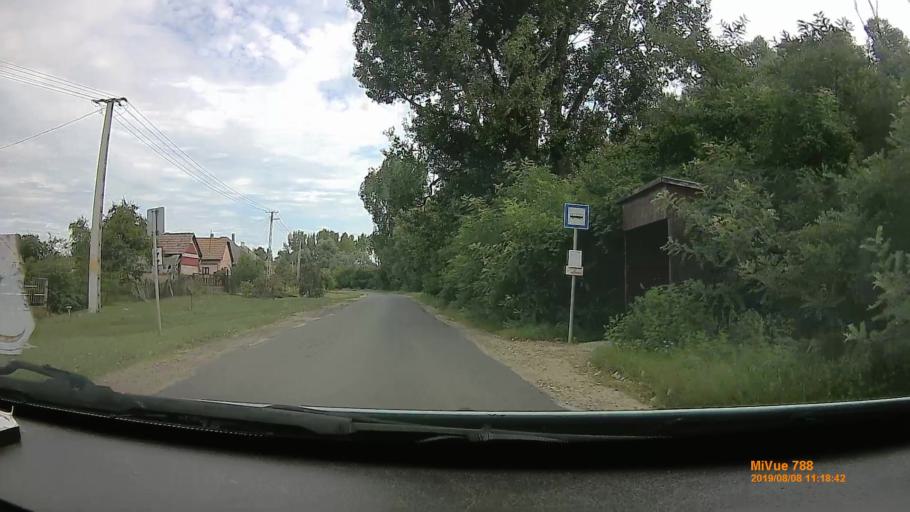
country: HU
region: Szabolcs-Szatmar-Bereg
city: Balkany
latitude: 47.7396
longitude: 21.8376
